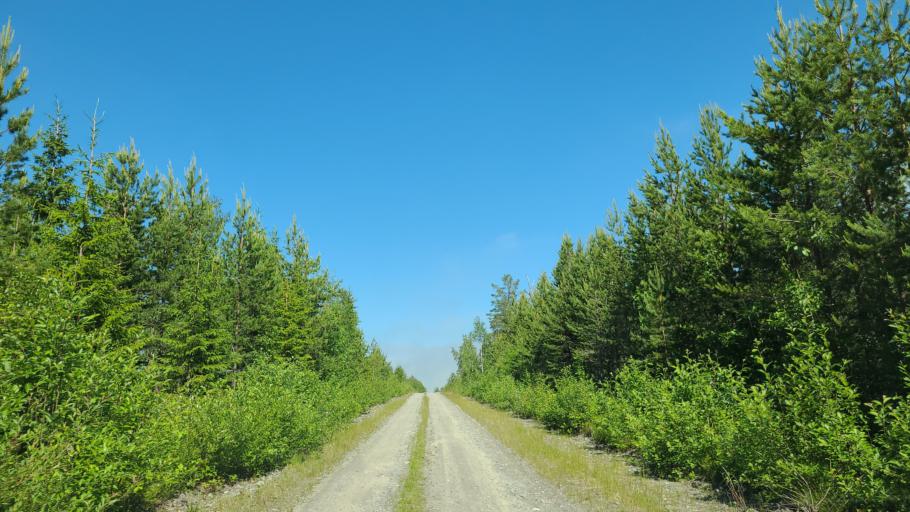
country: SE
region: Vaesternorrland
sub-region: OErnskoeldsviks Kommun
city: Husum
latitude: 63.4378
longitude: 19.2323
